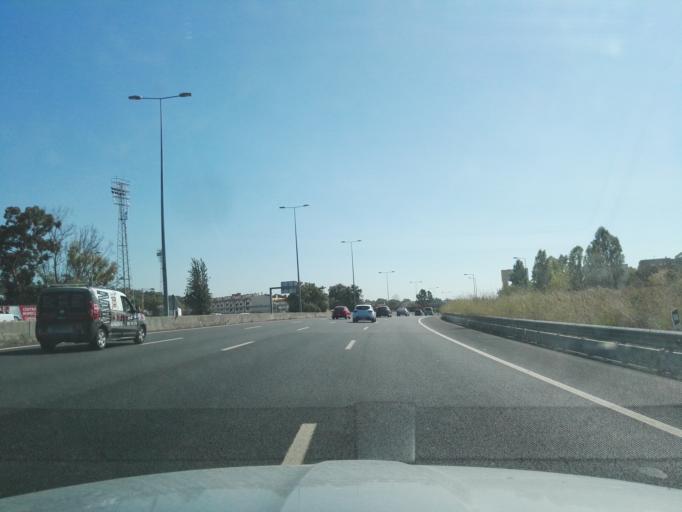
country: PT
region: Lisbon
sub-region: Odivelas
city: Pontinha
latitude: 38.7394
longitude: -9.2048
